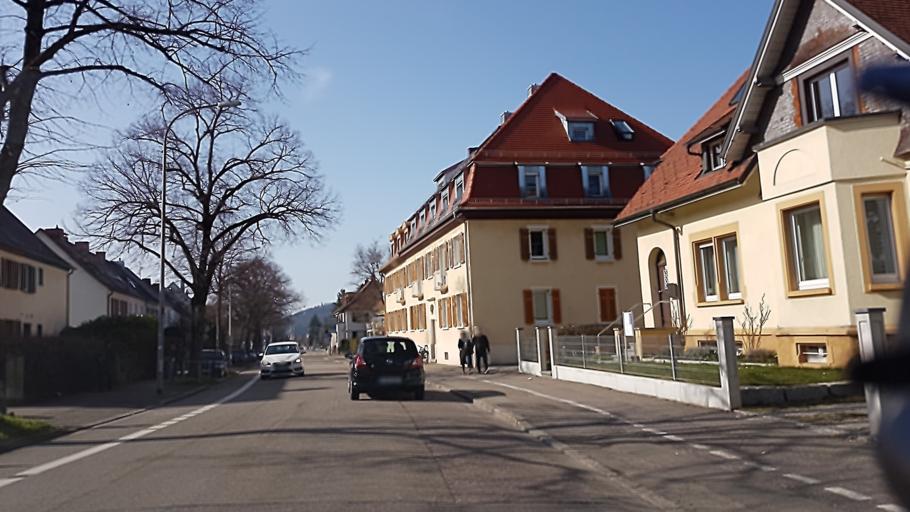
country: DE
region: Baden-Wuerttemberg
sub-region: Freiburg Region
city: Freiburg
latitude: 47.9839
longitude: 7.8968
